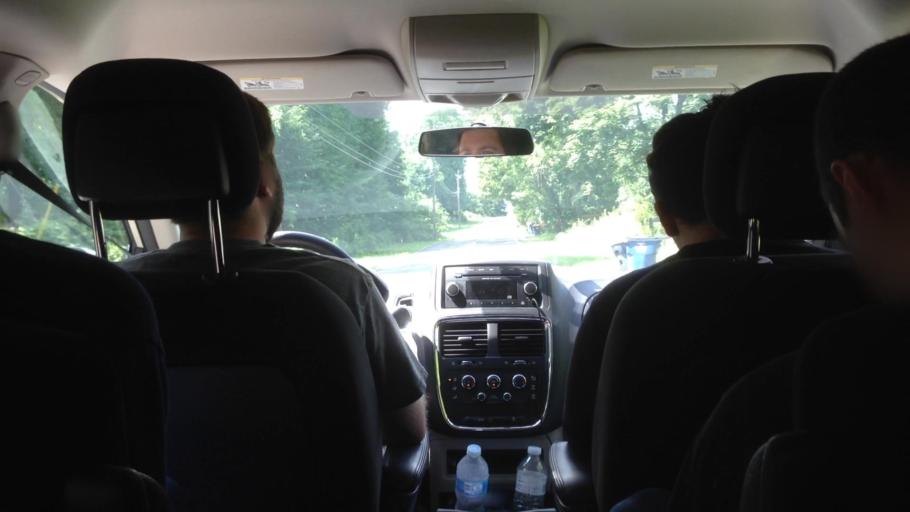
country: US
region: New York
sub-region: Dutchess County
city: Tivoli
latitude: 42.0543
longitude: -73.8865
